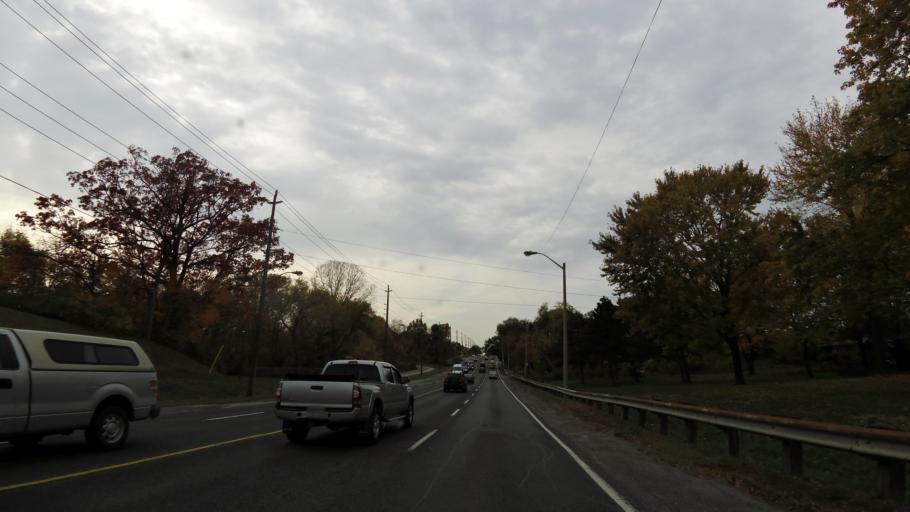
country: CA
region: Ontario
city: Etobicoke
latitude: 43.6818
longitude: -79.5298
